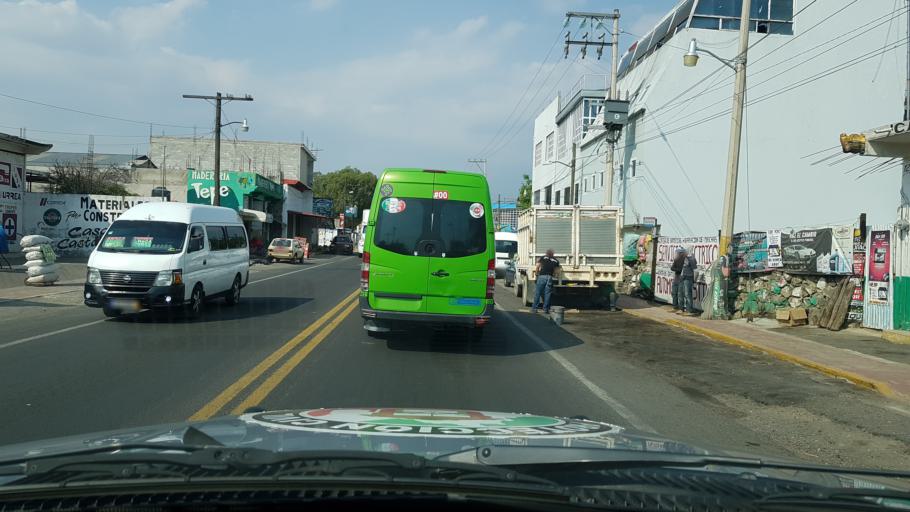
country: MX
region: Mexico
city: Tepetlixpa
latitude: 19.0268
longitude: -98.8164
